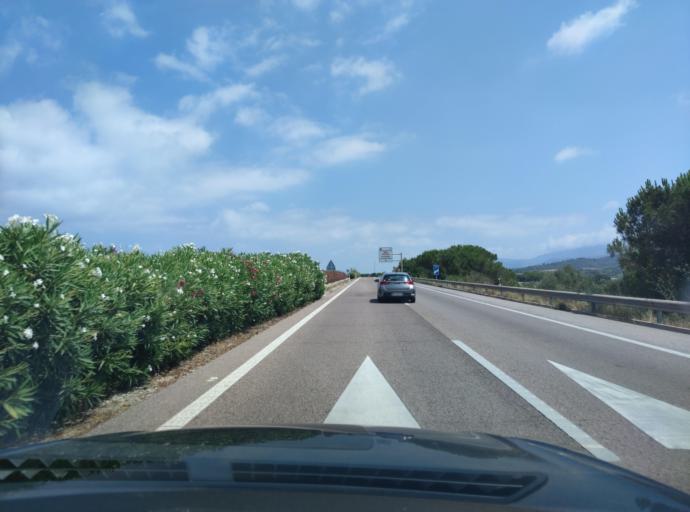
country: ES
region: Catalonia
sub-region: Provincia de Tarragona
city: Ulldecona
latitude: 40.5531
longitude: 0.4237
